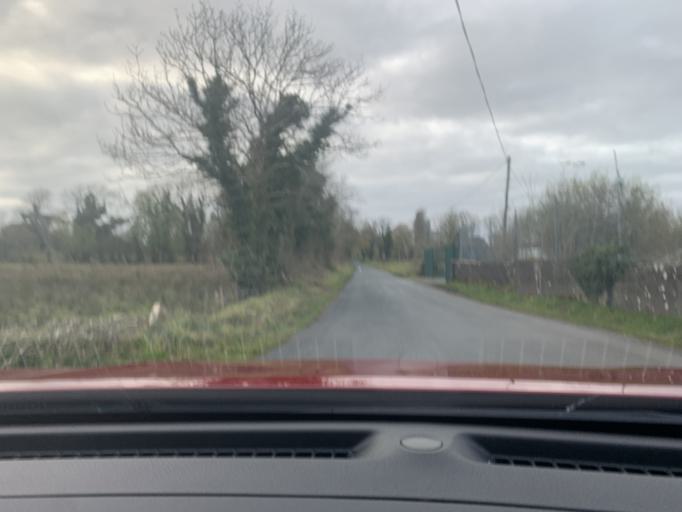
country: IE
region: Connaught
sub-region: Sligo
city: Tobercurry
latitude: 54.0211
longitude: -8.6359
